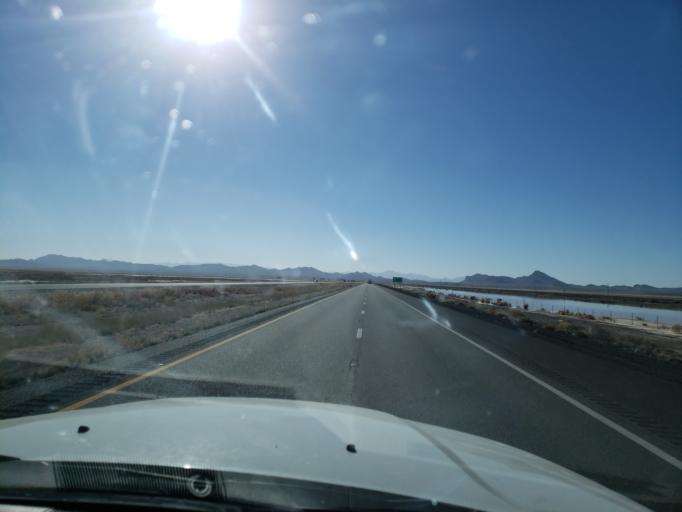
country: US
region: New Mexico
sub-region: Hidalgo County
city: Lordsburg
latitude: 32.2762
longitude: -108.8876
